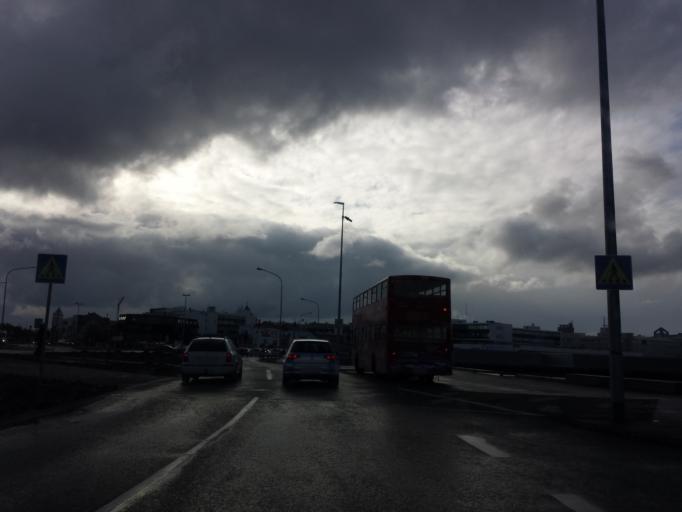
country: IS
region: Capital Region
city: Reykjavik
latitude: 64.1494
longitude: -21.9323
